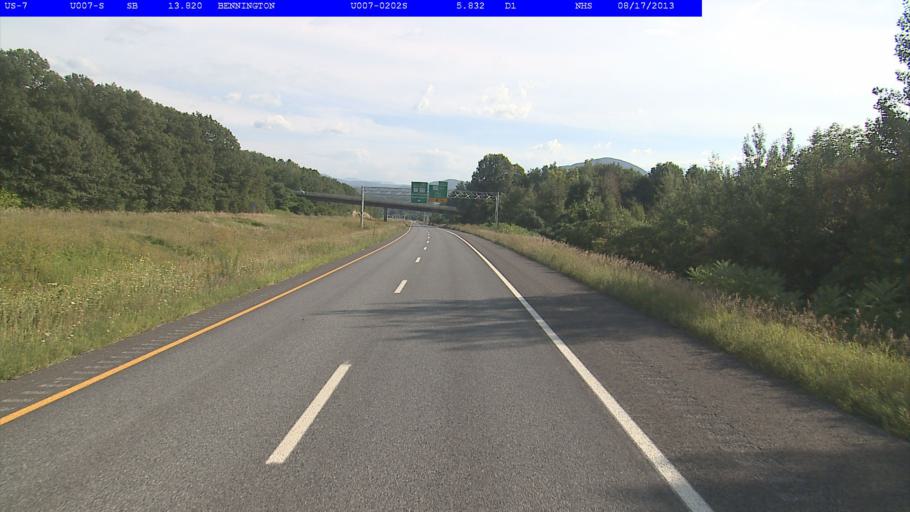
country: US
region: Vermont
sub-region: Bennington County
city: North Bennington
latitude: 42.9164
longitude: -73.2086
